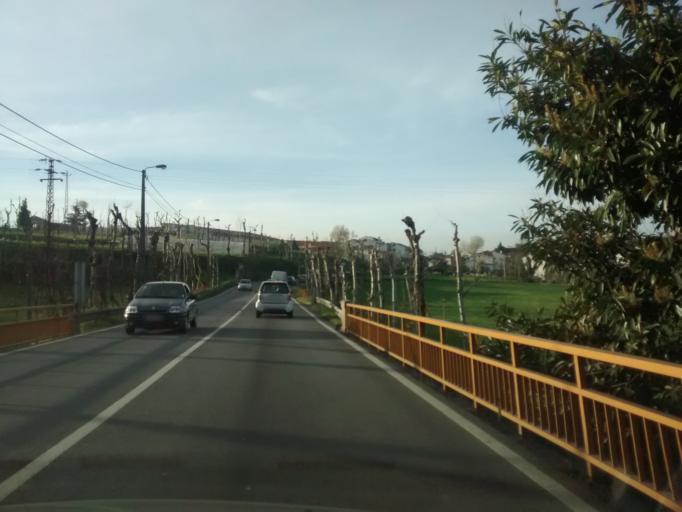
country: PT
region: Braga
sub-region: Guimaraes
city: Guimaraes
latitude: 41.4559
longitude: -8.3109
